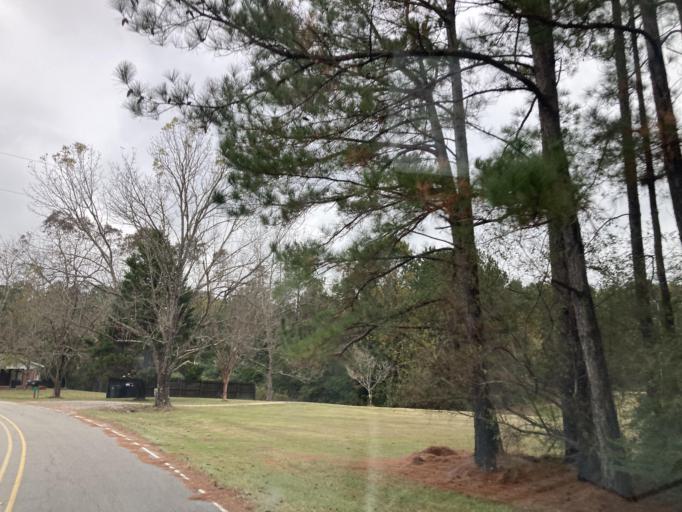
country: US
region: Mississippi
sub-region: Lamar County
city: Purvis
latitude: 31.1830
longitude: -89.4210
